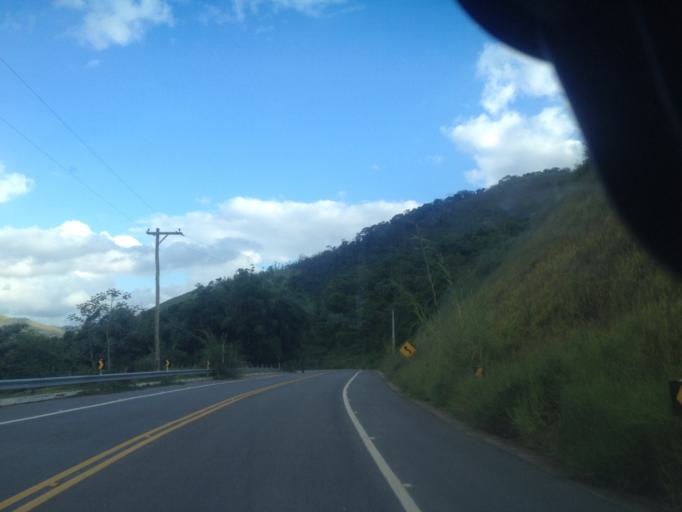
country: BR
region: Rio de Janeiro
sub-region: Quatis
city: Quatis
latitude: -22.2620
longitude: -44.2618
